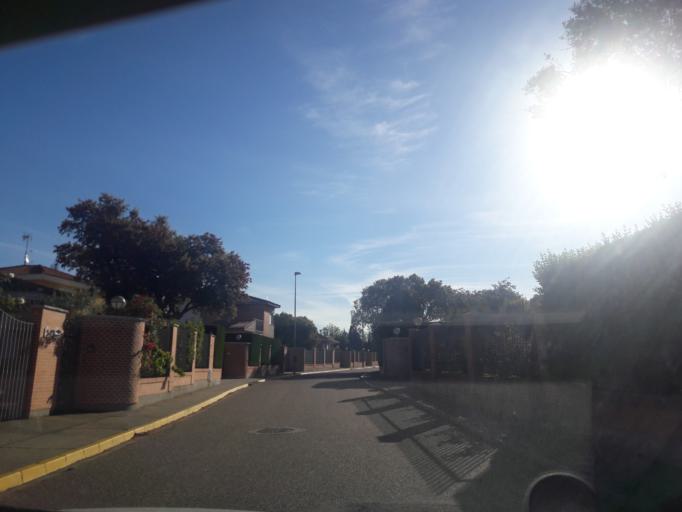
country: ES
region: Castille and Leon
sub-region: Provincia de Salamanca
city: Martinamor
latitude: 40.8096
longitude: -5.6348
